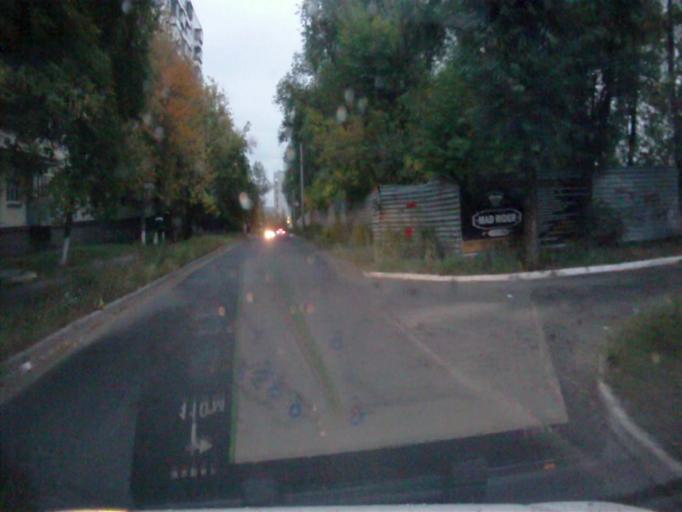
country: RU
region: Chelyabinsk
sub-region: Gorod Chelyabinsk
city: Chelyabinsk
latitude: 55.1910
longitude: 61.3358
